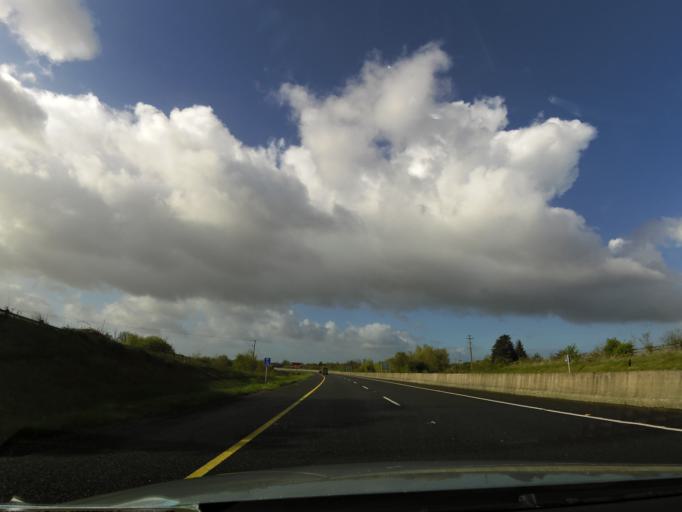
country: IE
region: Munster
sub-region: County Limerick
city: Castleconnell
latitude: 52.6933
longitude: -8.4971
